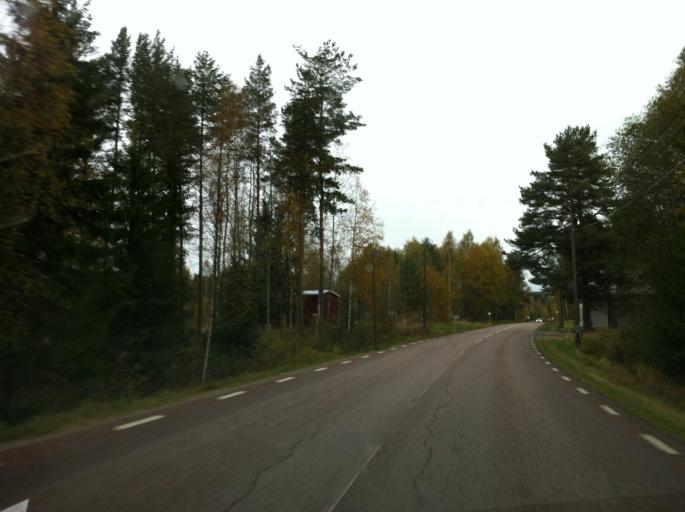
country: SE
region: Dalarna
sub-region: Ludvika Kommun
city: Grangesberg
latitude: 60.1476
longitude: 14.9852
